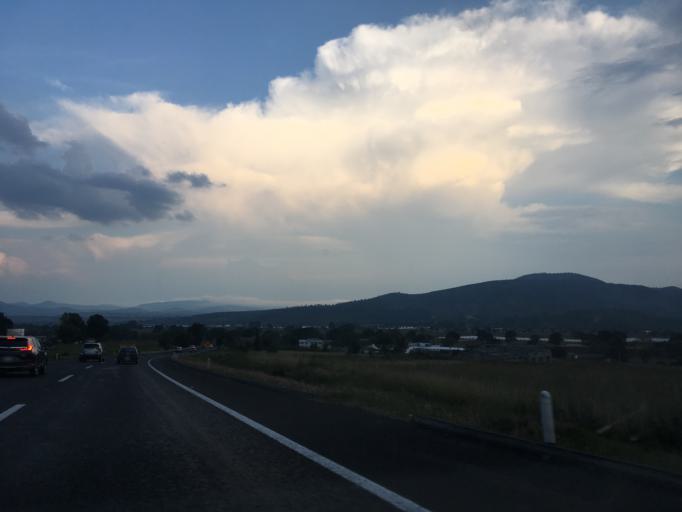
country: MX
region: Michoacan
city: Acuitzio del Canje
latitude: 19.5556
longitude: -101.3402
